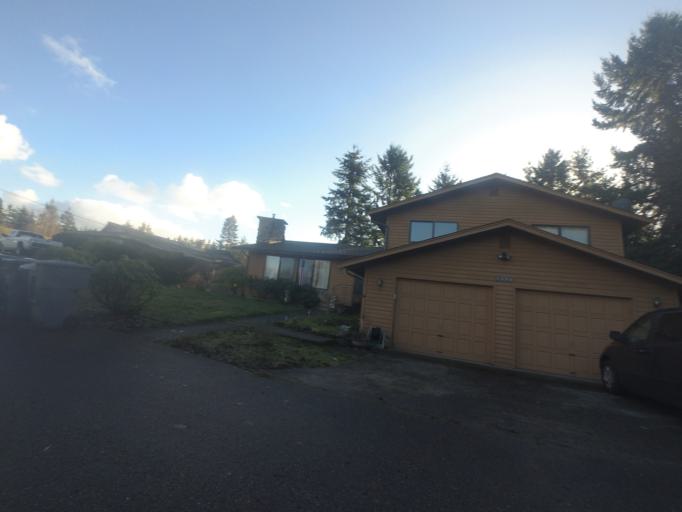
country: US
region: Washington
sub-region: Pierce County
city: University Place
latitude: 47.2262
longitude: -122.5422
